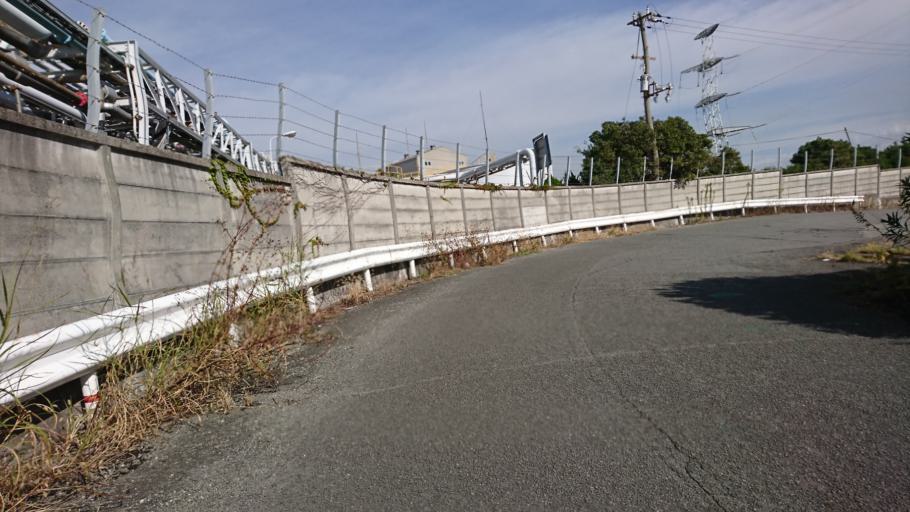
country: JP
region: Hyogo
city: Kakogawacho-honmachi
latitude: 34.7359
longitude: 134.7990
